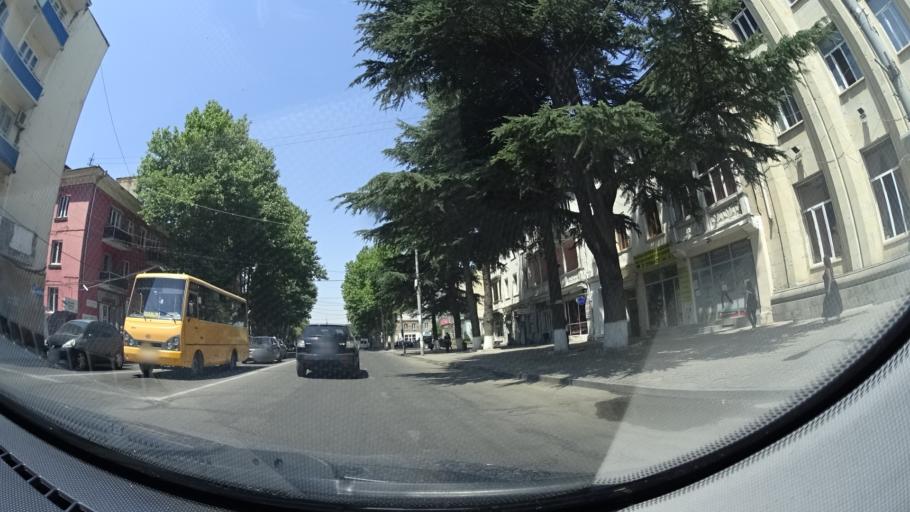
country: GE
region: Shida Kartli
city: Gori
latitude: 41.9830
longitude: 44.1122
